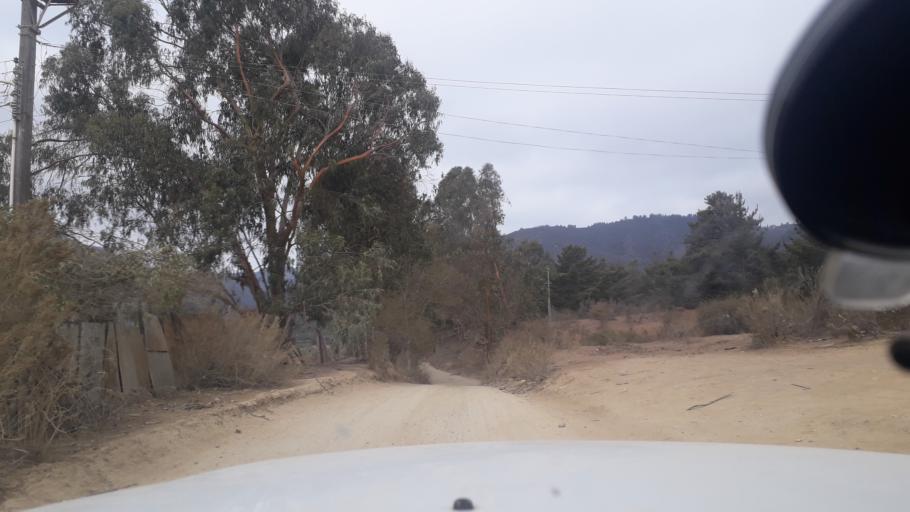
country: CL
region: Valparaiso
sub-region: Provincia de Valparaiso
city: Valparaiso
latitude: -33.1155
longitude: -71.6418
